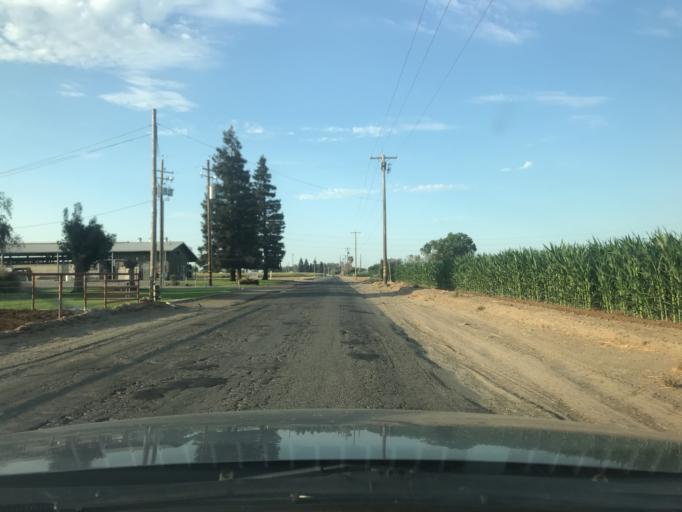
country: US
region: California
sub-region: Merced County
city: Atwater
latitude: 37.3523
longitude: -120.5496
